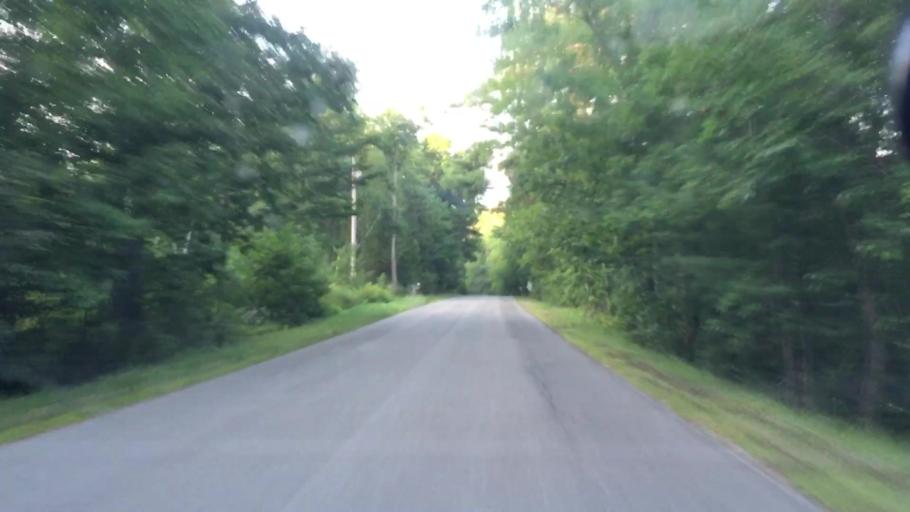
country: US
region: Maine
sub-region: Waldo County
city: Frankfort
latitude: 44.6642
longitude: -68.9271
